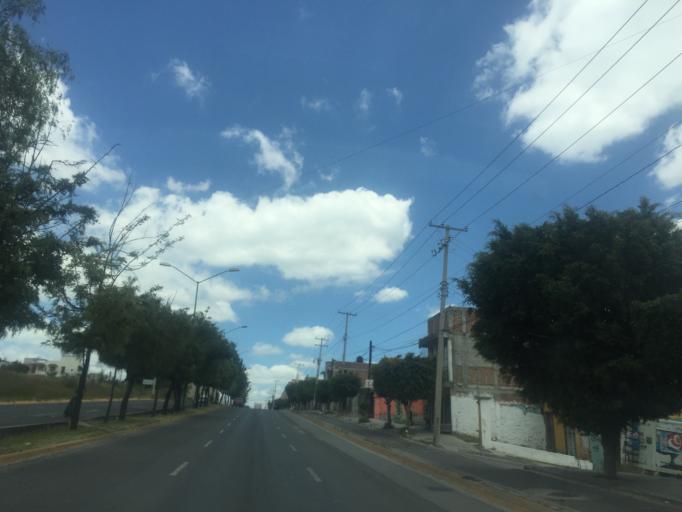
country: MX
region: Guanajuato
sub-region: Leon
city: Ejido la Joya
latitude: 21.1246
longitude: -101.7197
